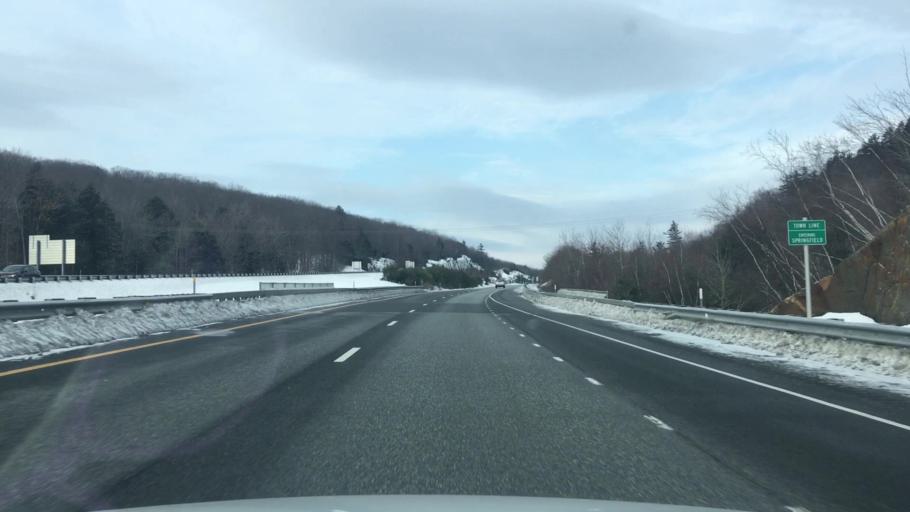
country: US
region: New Hampshire
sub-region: Sullivan County
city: Sunapee
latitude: 43.4432
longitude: -72.0717
